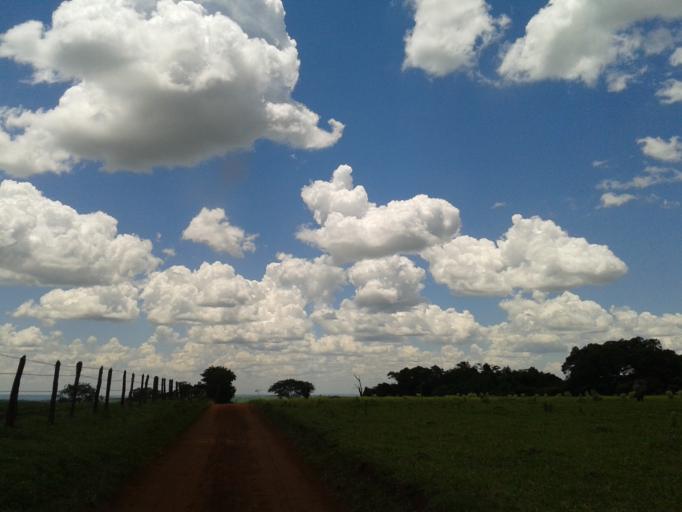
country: BR
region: Minas Gerais
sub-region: Centralina
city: Centralina
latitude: -18.6964
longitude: -49.1897
